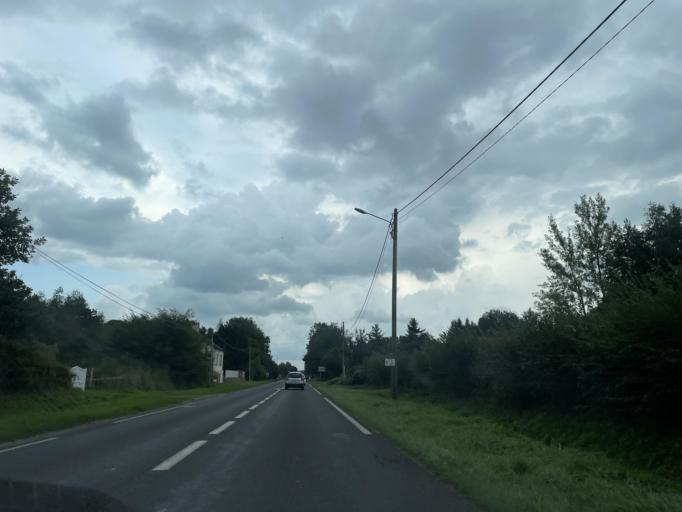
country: FR
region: Haute-Normandie
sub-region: Departement de la Seine-Maritime
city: Gournay-en-Bray
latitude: 49.5079
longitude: 1.6668
